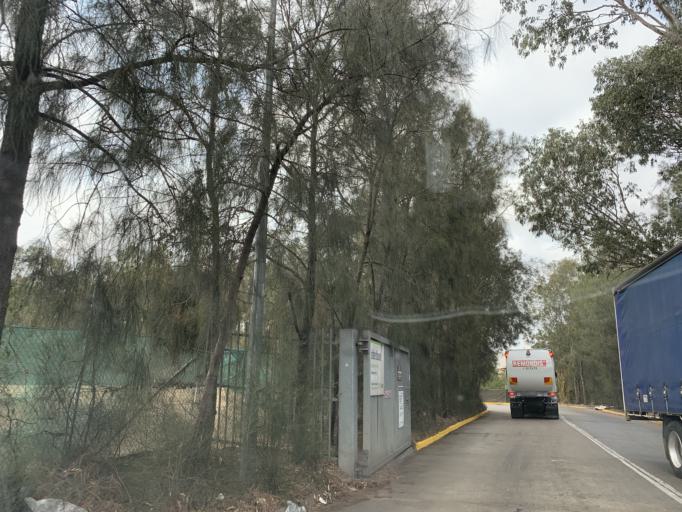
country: AU
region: New South Wales
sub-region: Holroyd
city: Girraween
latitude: -33.7750
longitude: 150.9509
